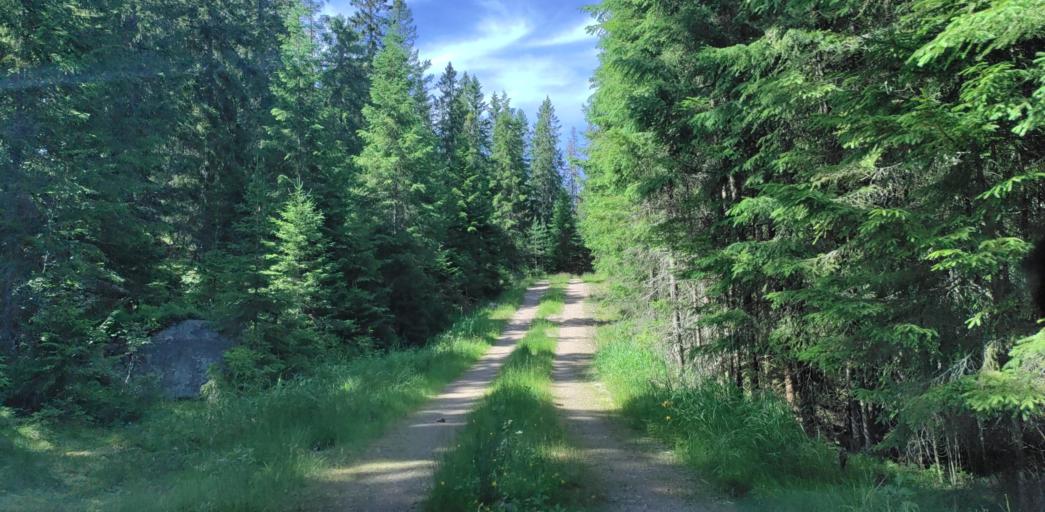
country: SE
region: Vaermland
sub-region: Hagfors Kommun
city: Ekshaerad
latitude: 60.0878
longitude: 13.3778
